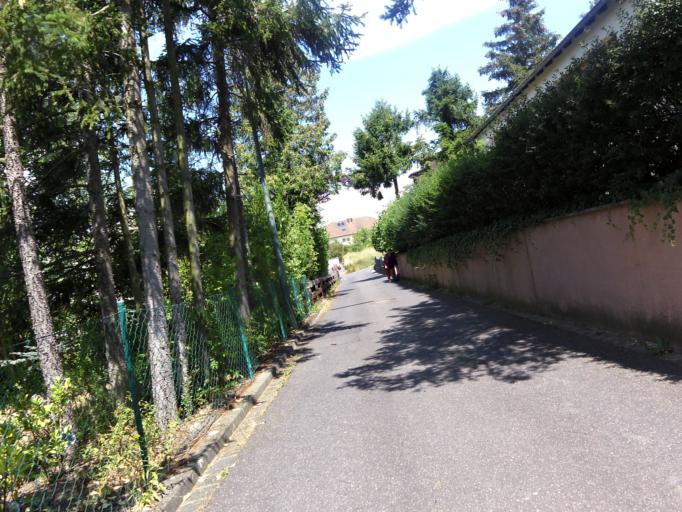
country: DE
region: Bavaria
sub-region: Regierungsbezirk Unterfranken
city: Wuerzburg
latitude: 49.8167
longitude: 9.9712
